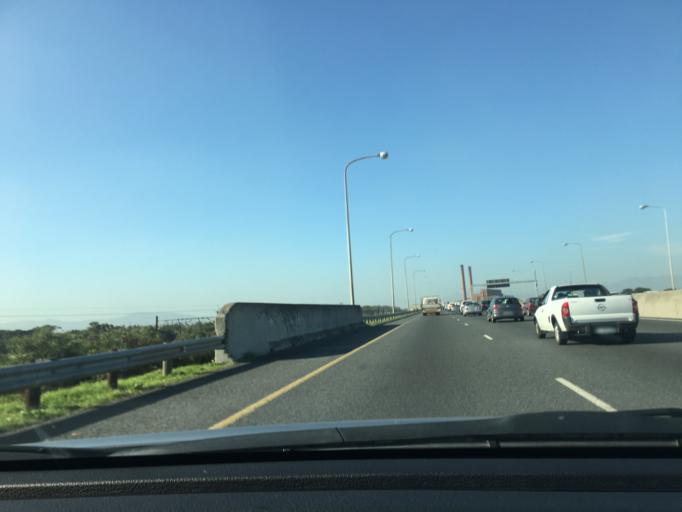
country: ZA
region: Western Cape
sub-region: City of Cape Town
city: Rosebank
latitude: -33.9505
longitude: 18.4990
